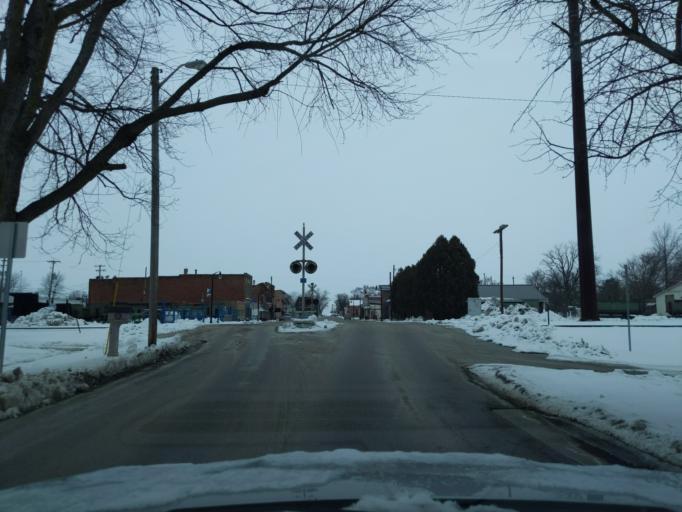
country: US
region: Indiana
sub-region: Benton County
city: Otterbein
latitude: 40.4882
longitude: -87.0962
